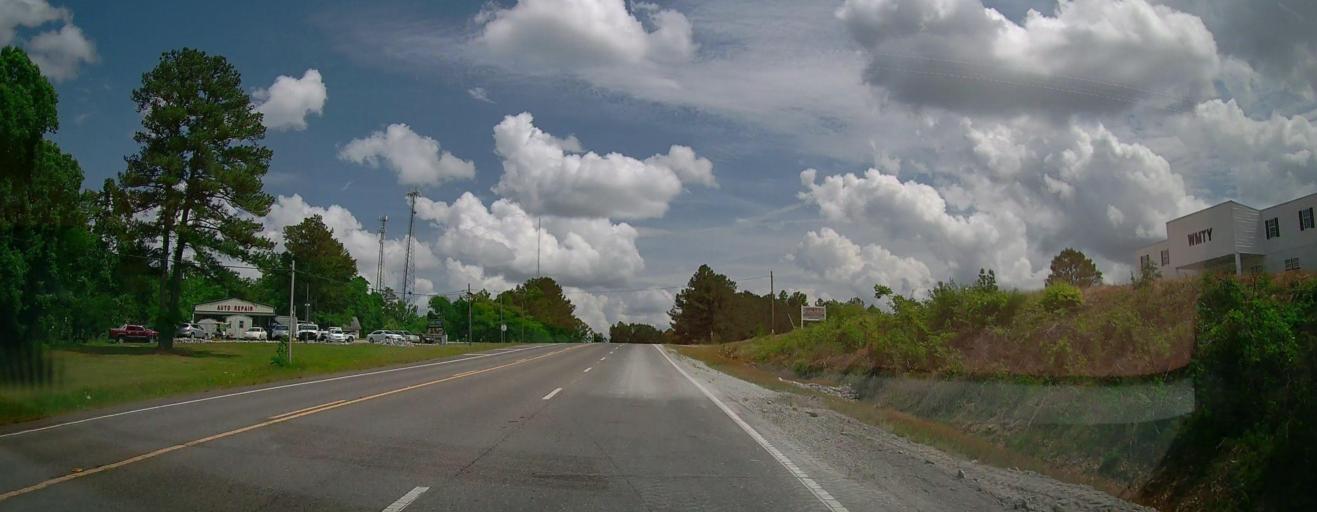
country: US
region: Alabama
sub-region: Marion County
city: Hamilton
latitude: 34.0847
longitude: -87.9787
